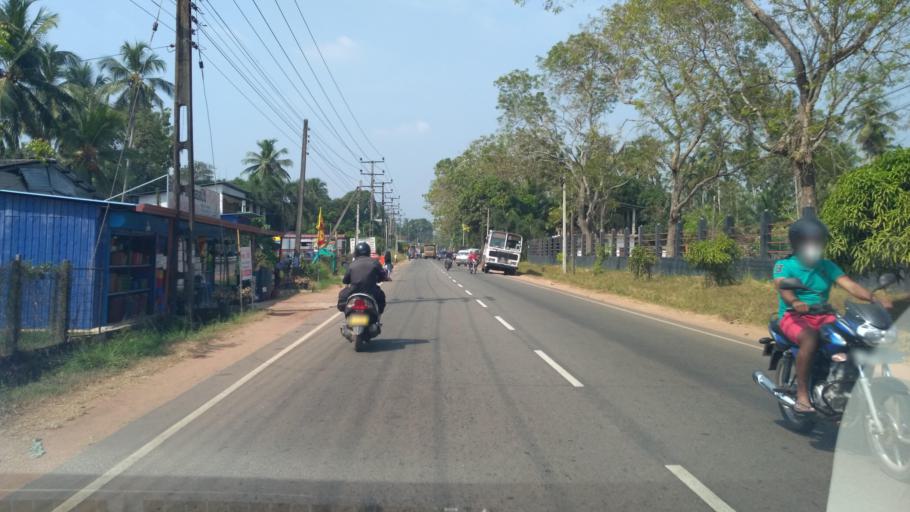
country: LK
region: Western
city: Minuwangoda
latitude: 7.3206
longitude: 79.9725
